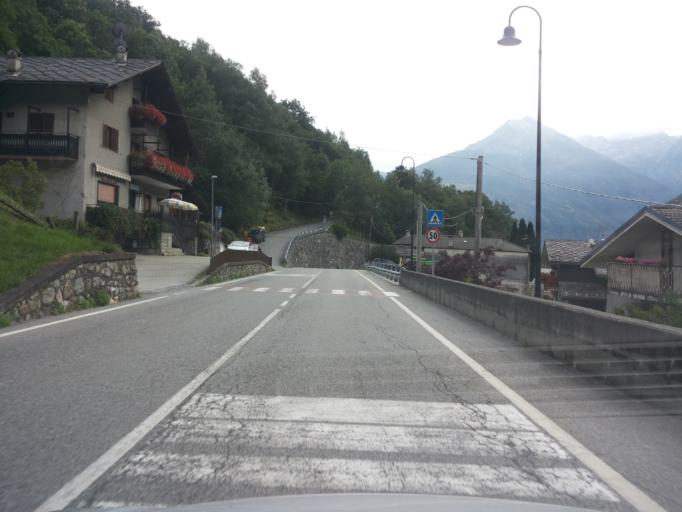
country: IT
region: Aosta Valley
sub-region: Valle d'Aosta
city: Perloz
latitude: 45.6181
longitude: 7.8182
